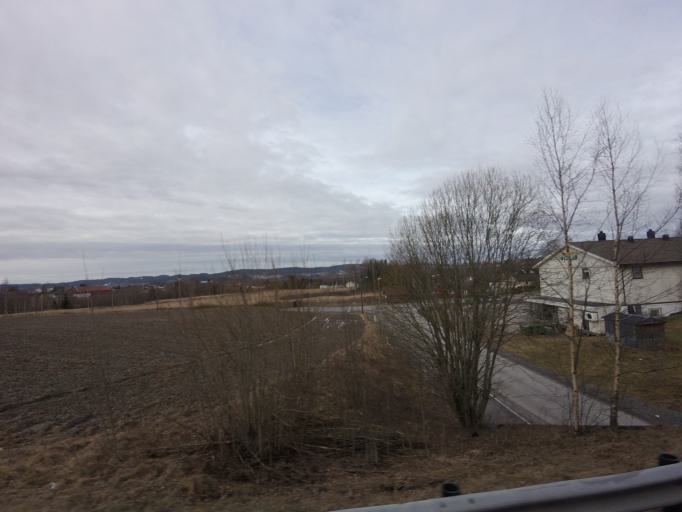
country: NO
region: Akershus
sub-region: Fet
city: Fetsund
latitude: 59.9197
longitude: 11.1832
